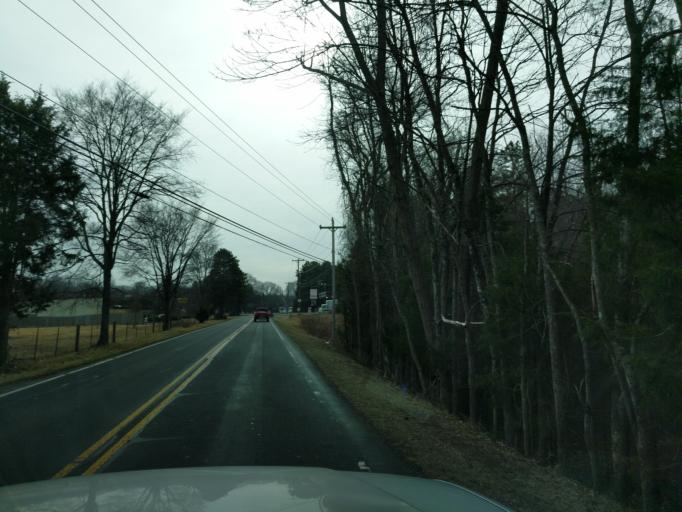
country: US
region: North Carolina
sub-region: Mecklenburg County
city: Huntersville
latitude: 35.3247
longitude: -80.9038
